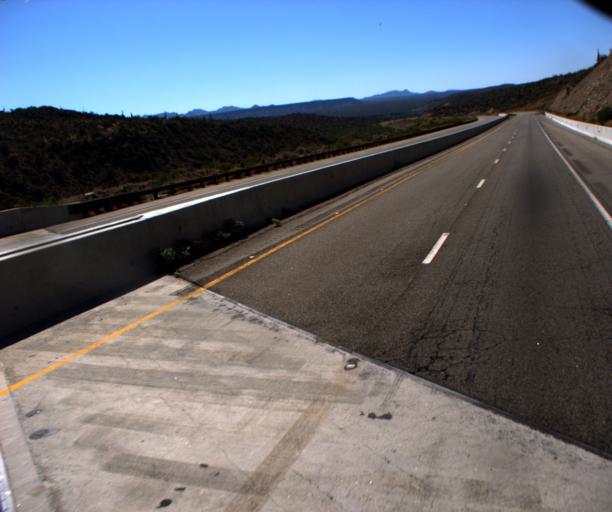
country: US
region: Arizona
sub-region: Yavapai County
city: Bagdad
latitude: 34.4028
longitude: -113.2206
